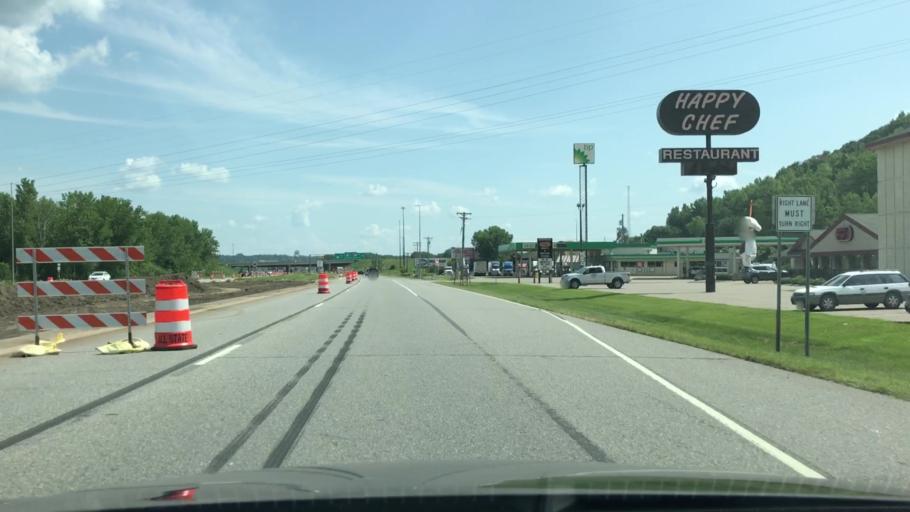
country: US
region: Minnesota
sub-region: Nicollet County
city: North Mankato
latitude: 44.1972
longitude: -94.0206
